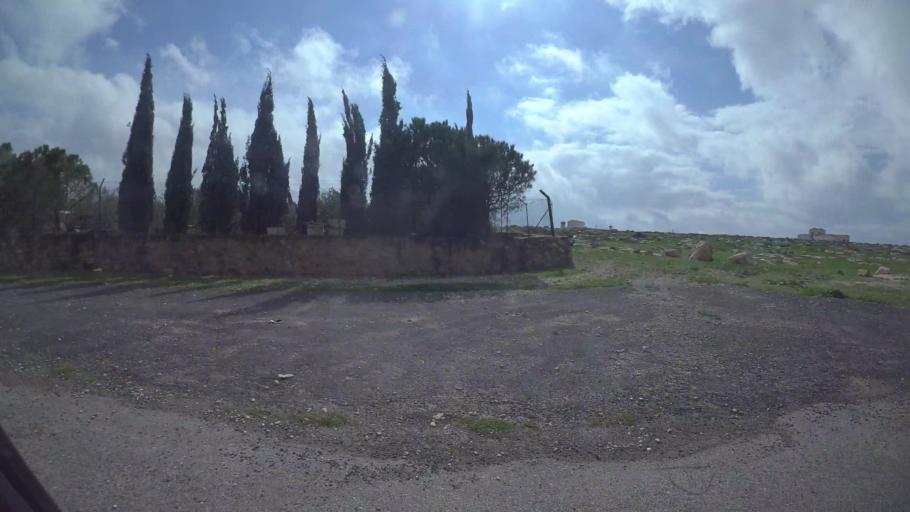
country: JO
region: Amman
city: Al Jubayhah
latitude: 32.0771
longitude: 35.8867
